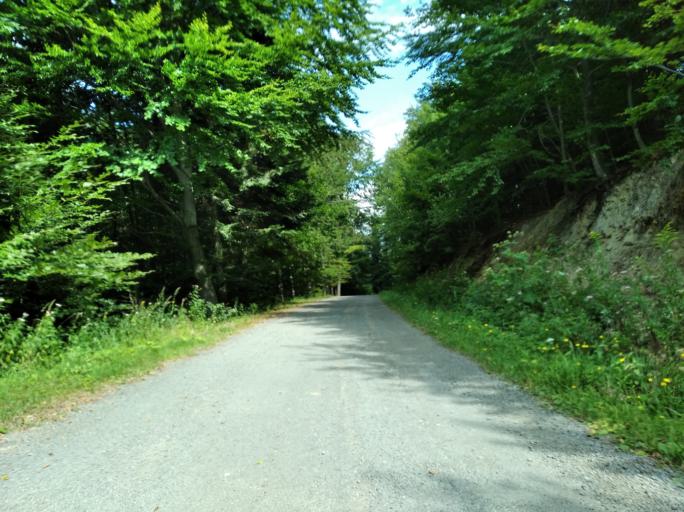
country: PL
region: Subcarpathian Voivodeship
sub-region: Powiat krosnienski
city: Leki
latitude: 49.8398
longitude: 21.6668
